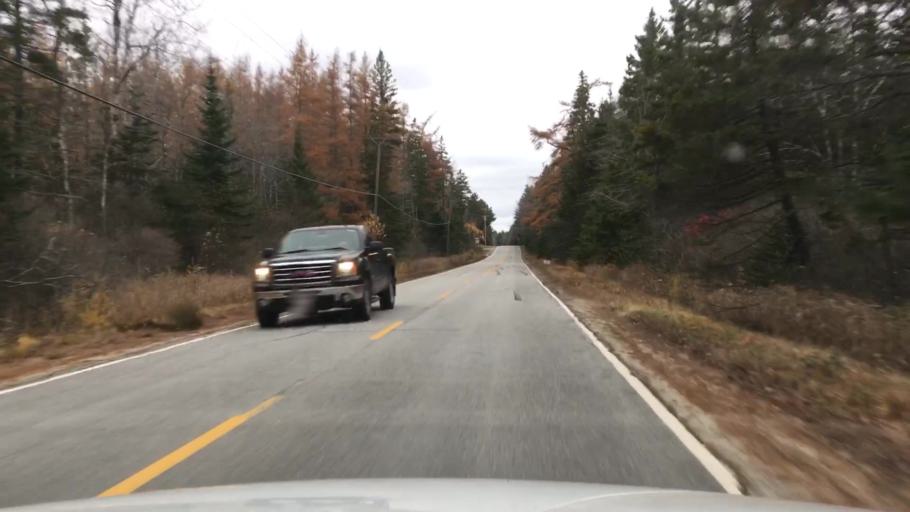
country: US
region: Maine
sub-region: Hancock County
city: Sedgwick
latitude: 44.2804
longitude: -68.5539
